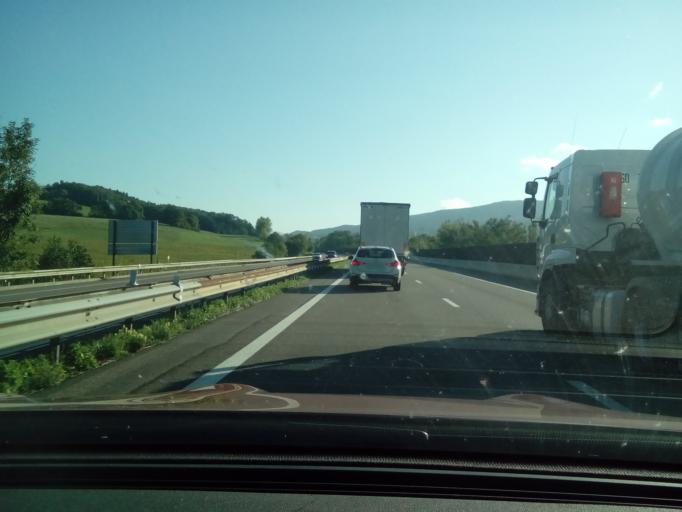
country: FR
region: Rhone-Alpes
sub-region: Departement de la Haute-Savoie
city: Alby-sur-Cheran
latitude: 45.8267
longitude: 6.0342
